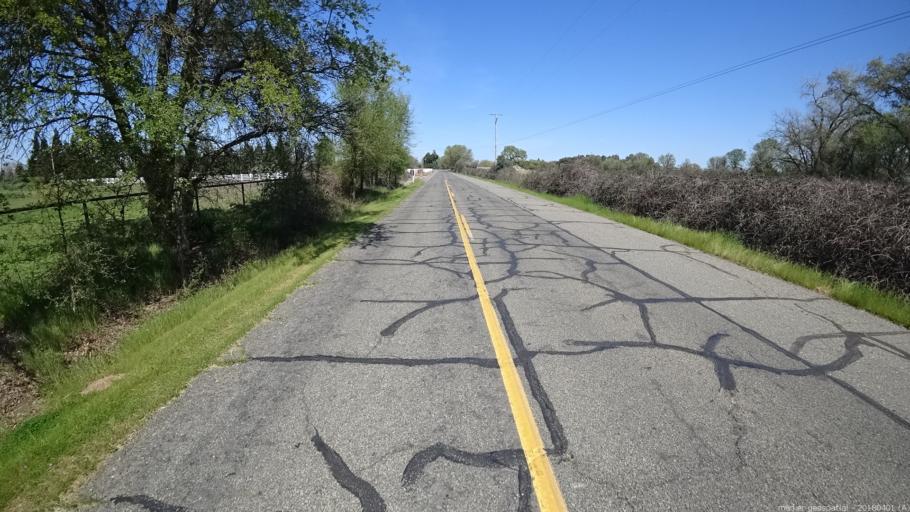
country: US
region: California
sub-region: Sacramento County
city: Wilton
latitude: 38.4320
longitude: -121.1951
